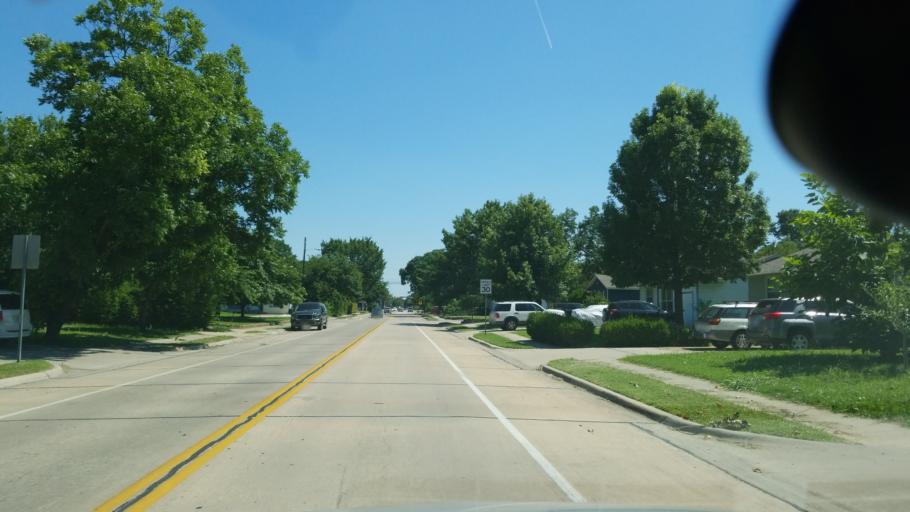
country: US
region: Texas
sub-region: Dallas County
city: Irving
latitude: 32.8322
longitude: -96.9354
